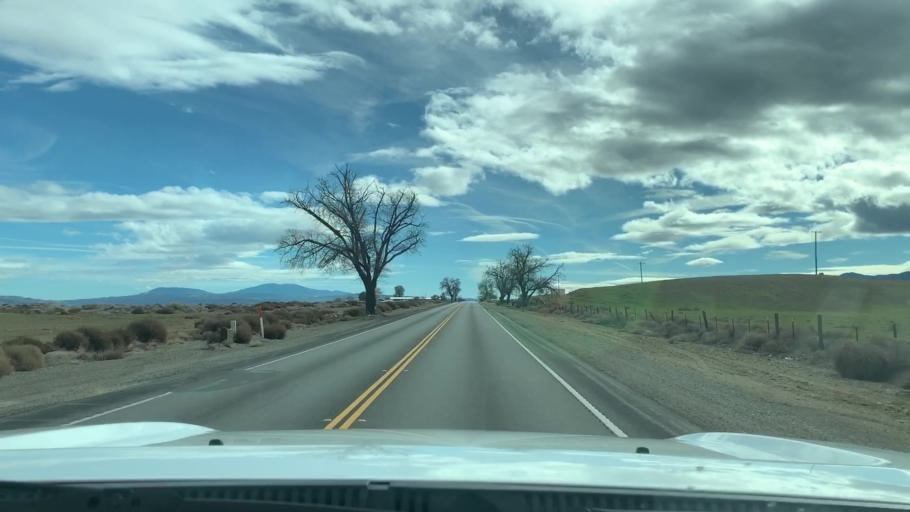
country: US
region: California
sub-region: Kern County
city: Taft Heights
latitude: 34.9640
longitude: -119.7214
